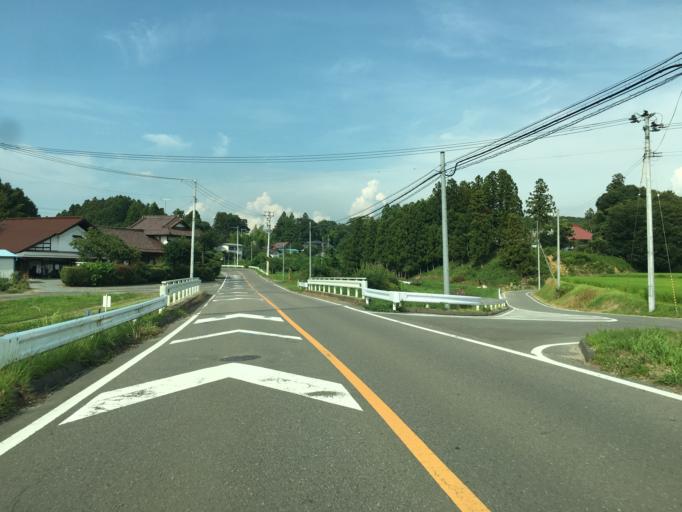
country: JP
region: Fukushima
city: Koriyama
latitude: 37.3502
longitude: 140.4144
